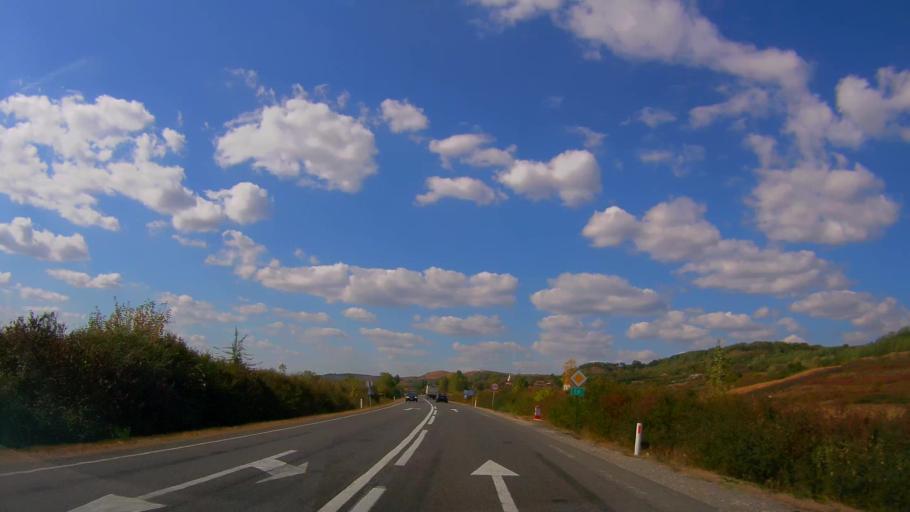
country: RO
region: Salaj
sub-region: Comuna Bocsa
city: Bocsa
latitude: 47.3136
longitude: 22.9127
